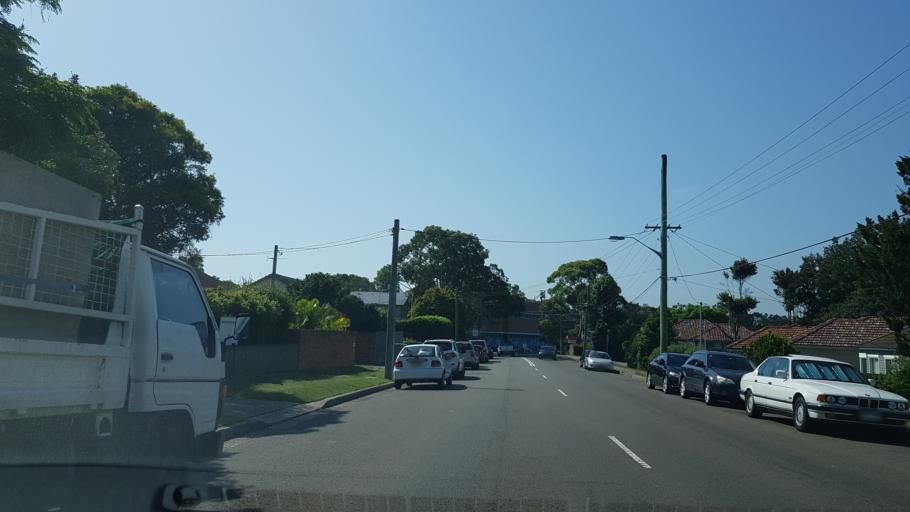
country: AU
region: New South Wales
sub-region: Warringah
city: Dee Why
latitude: -33.7433
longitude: 151.2931
